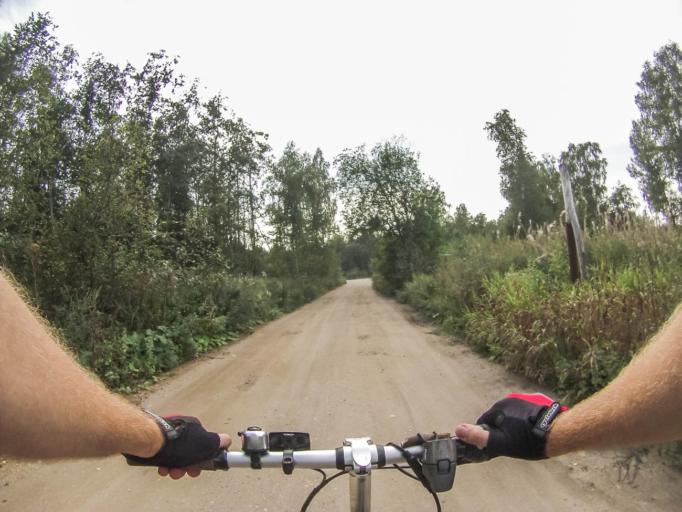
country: RU
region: Jaroslavl
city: Uglich
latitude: 57.4838
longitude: 38.3680
